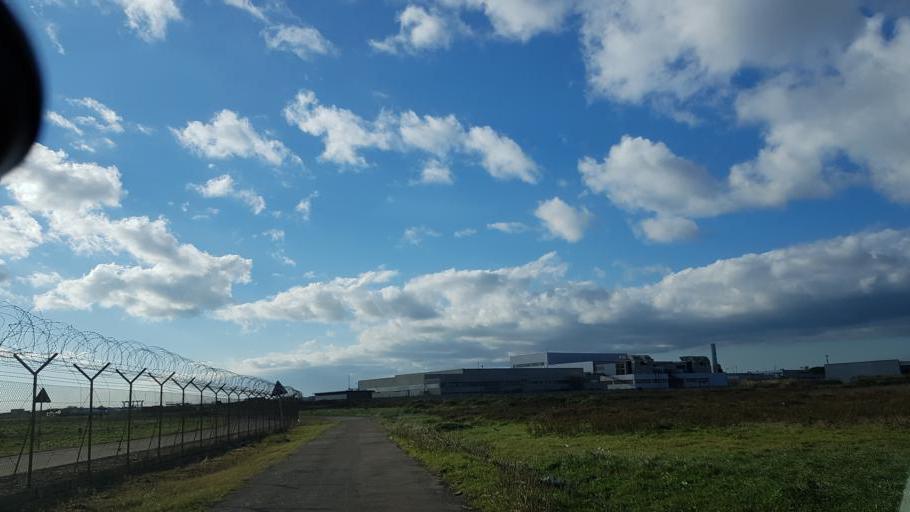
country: IT
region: Apulia
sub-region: Provincia di Brindisi
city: Materdomini
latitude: 40.6766
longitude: 17.9223
